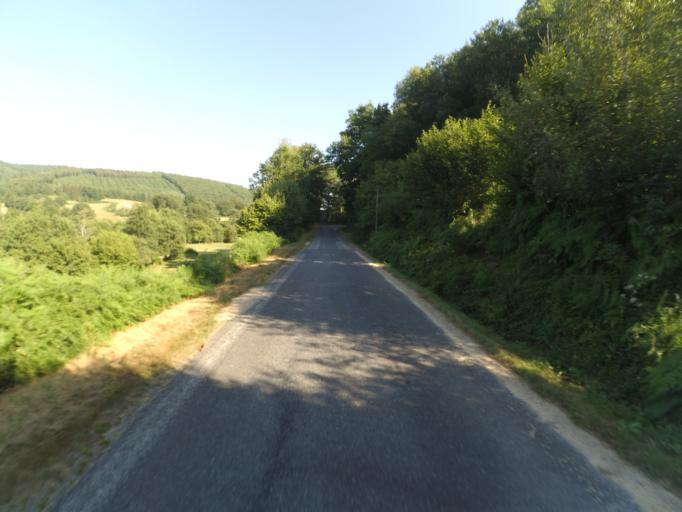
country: FR
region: Limousin
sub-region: Departement de la Haute-Vienne
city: Eymoutiers
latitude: 45.7252
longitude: 1.8249
